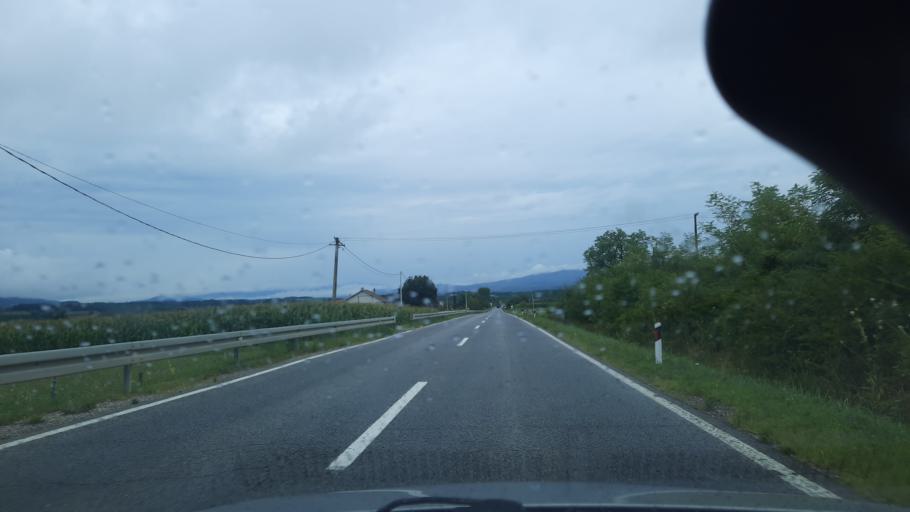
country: RS
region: Central Serbia
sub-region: Sumadijski Okrug
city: Knic
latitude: 43.9287
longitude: 20.7745
